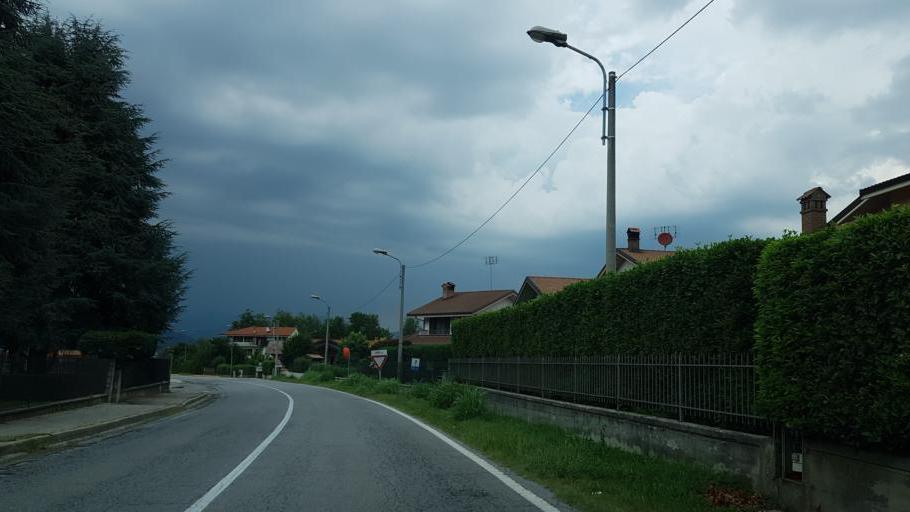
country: IT
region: Piedmont
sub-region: Provincia di Cuneo
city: Cervasca
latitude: 44.3839
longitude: 7.4671
